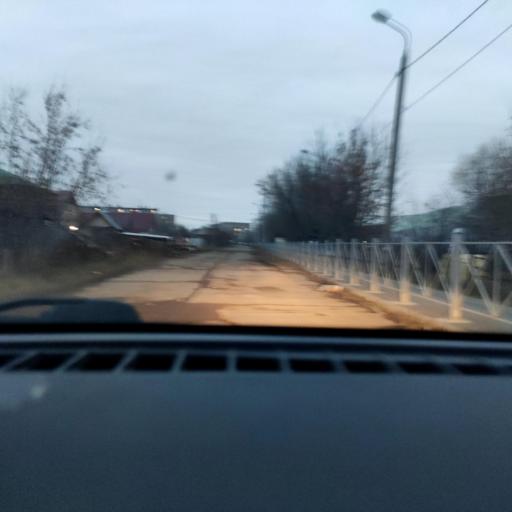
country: RU
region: Perm
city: Kondratovo
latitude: 57.9622
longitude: 56.1449
